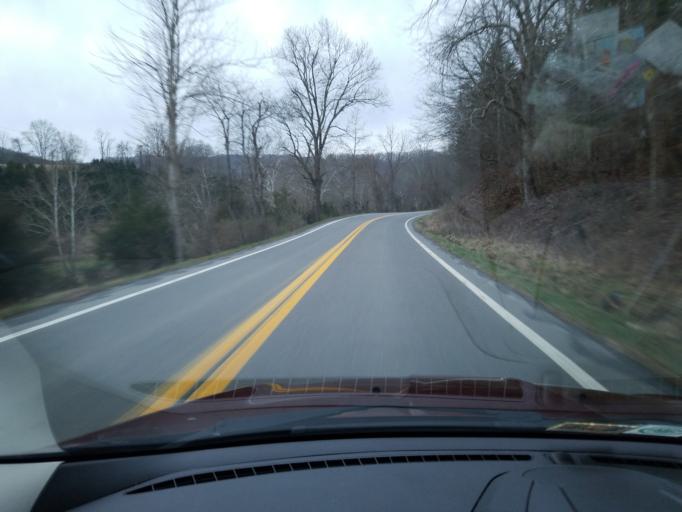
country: US
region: West Virginia
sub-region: Monroe County
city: Union
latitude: 37.5642
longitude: -80.5686
